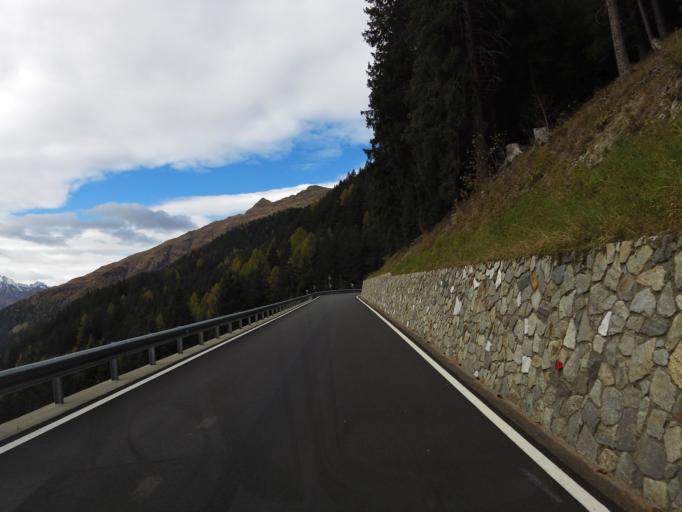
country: IT
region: Trentino-Alto Adige
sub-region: Bolzano
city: Racines
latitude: 46.8275
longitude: 11.3071
